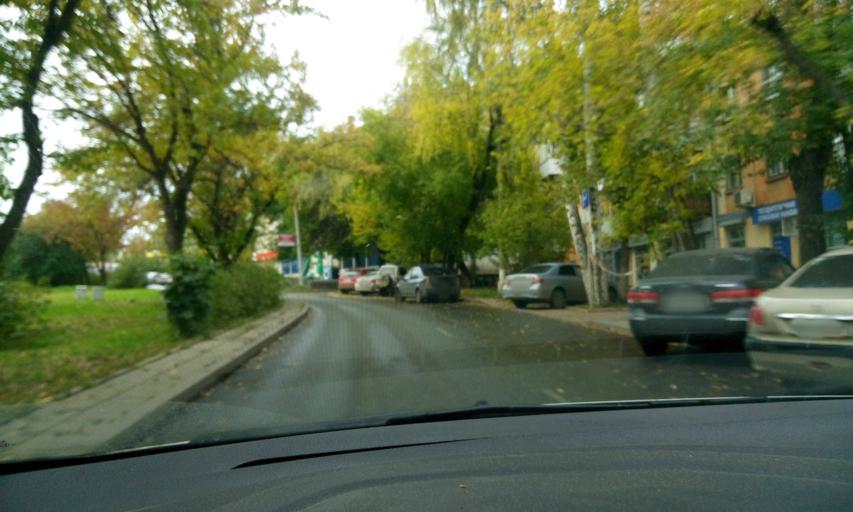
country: RU
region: Sverdlovsk
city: Yekaterinburg
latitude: 56.8523
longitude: 60.6474
